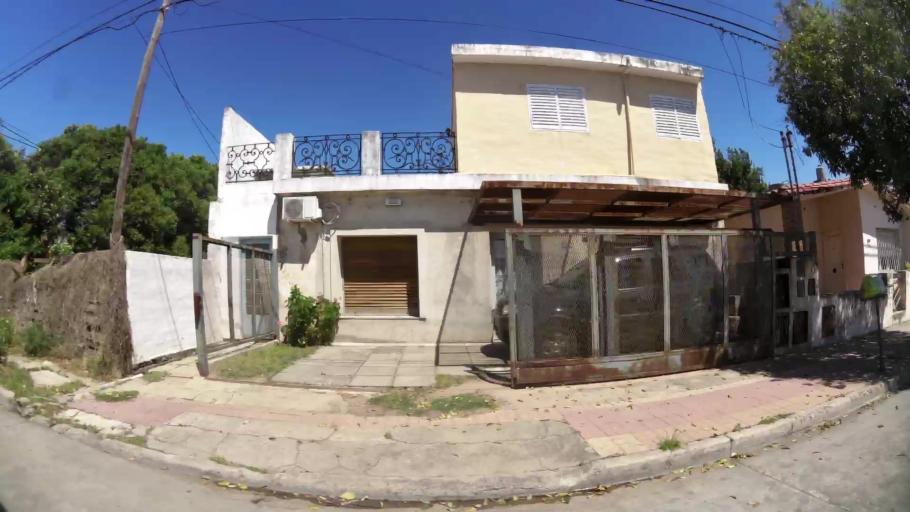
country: AR
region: Cordoba
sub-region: Departamento de Capital
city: Cordoba
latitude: -31.4243
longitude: -64.2074
